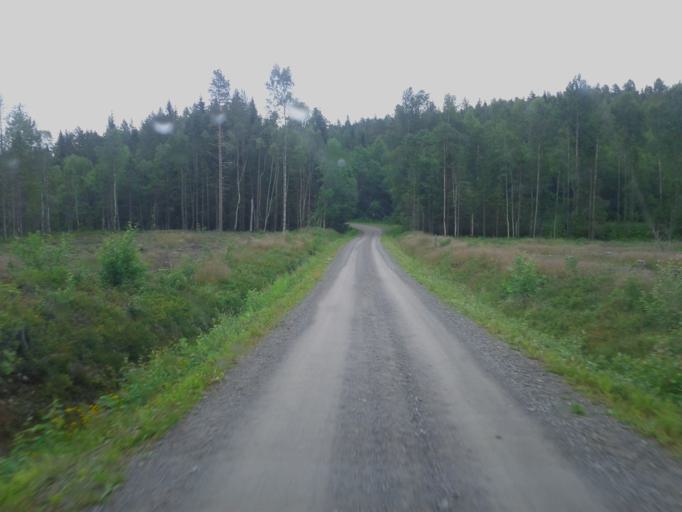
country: SE
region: Vaesternorrland
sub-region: OErnskoeldsviks Kommun
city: Bjasta
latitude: 63.0754
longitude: 18.4496
